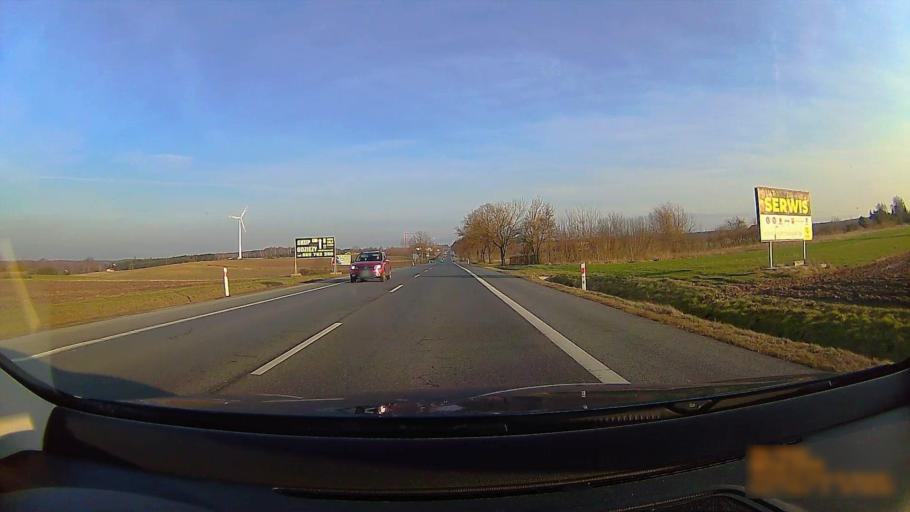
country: PL
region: Greater Poland Voivodeship
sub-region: Konin
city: Konin
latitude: 52.1934
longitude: 18.3193
